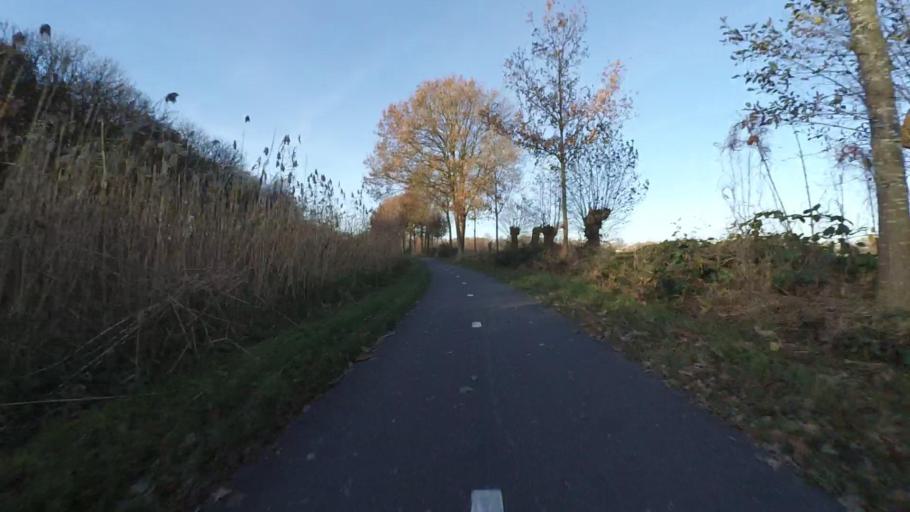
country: NL
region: Utrecht
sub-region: Gemeente Utrechtse Heuvelrug
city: Overberg
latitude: 52.0749
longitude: 5.4703
